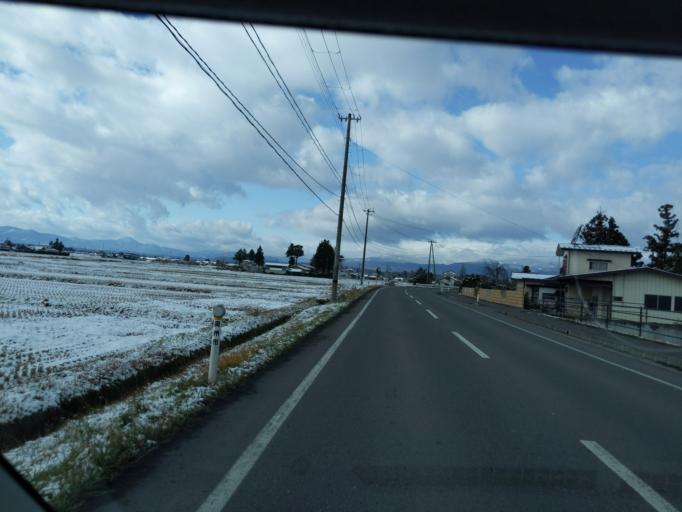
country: JP
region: Iwate
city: Mizusawa
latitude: 39.1624
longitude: 141.1077
